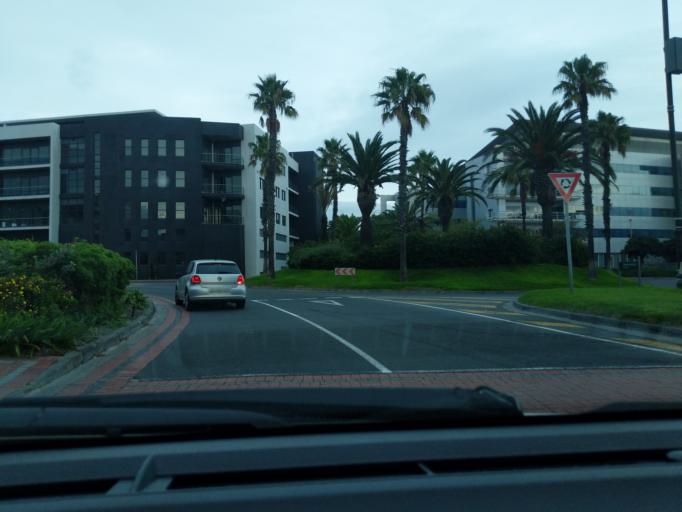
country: ZA
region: Western Cape
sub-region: City of Cape Town
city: Sunset Beach
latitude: -33.8851
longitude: 18.5199
